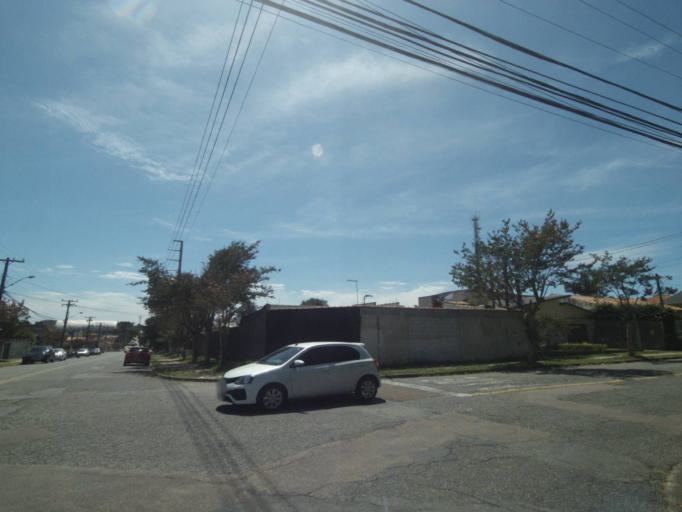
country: BR
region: Parana
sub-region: Curitiba
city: Curitiba
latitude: -25.4599
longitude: -49.2403
